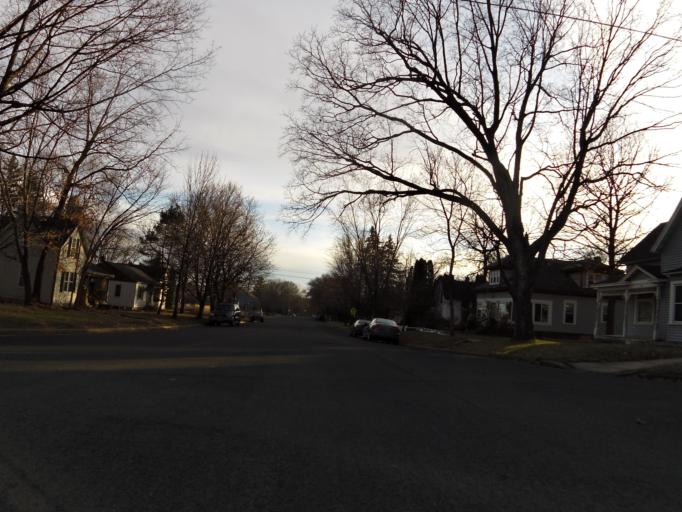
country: US
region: Wisconsin
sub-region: Pierce County
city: River Falls
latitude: 44.8617
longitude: -92.6281
